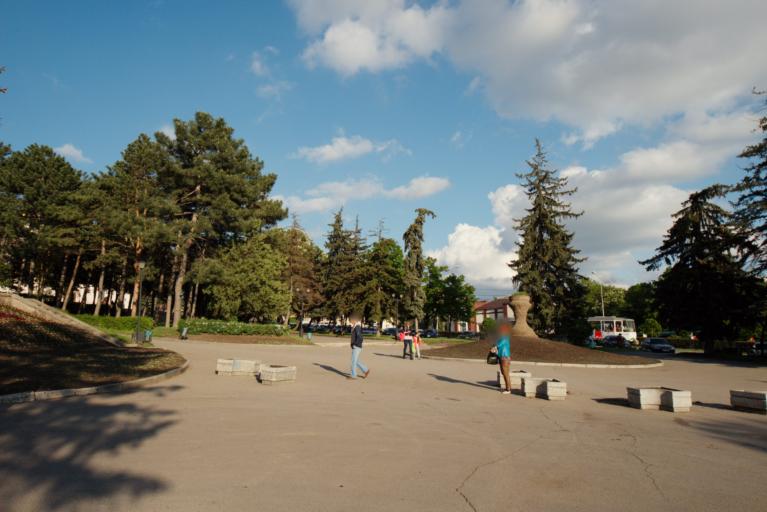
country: RU
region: Stavropol'skiy
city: Pyatigorsk
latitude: 44.0370
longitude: 43.0764
